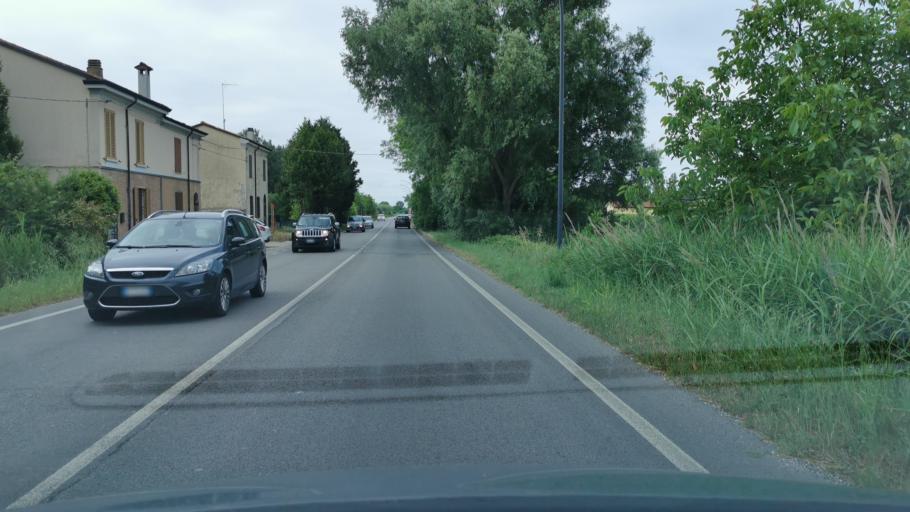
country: IT
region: Emilia-Romagna
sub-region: Provincia di Ravenna
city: Madonna Dell'Albero
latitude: 44.3950
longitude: 12.1972
